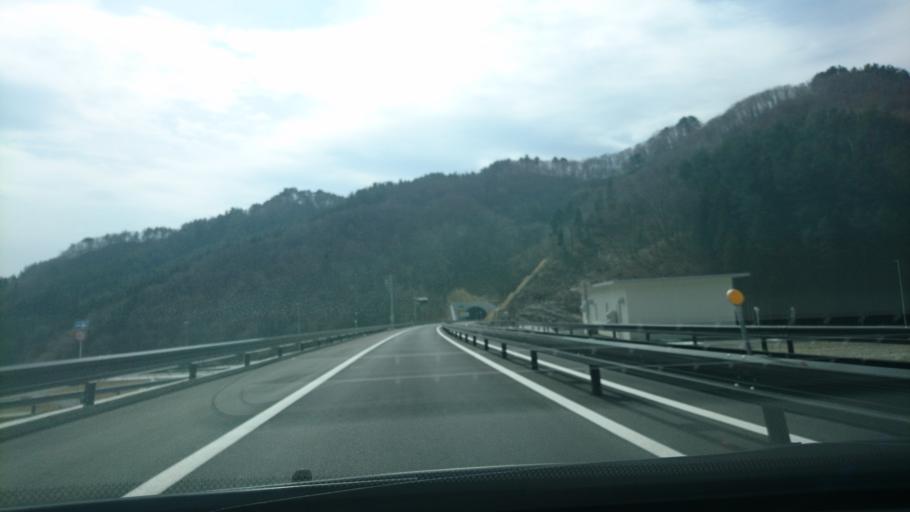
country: JP
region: Iwate
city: Kamaishi
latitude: 39.2193
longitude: 141.8671
